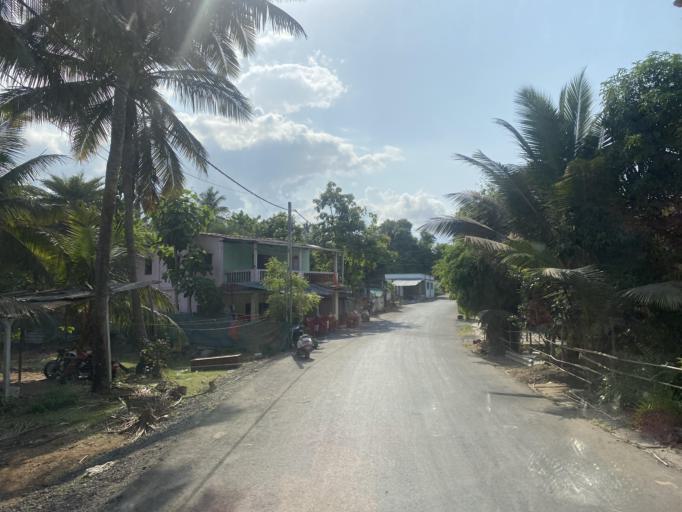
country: IN
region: Daman and Diu
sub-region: Daman District
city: Daman
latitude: 20.3774
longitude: 72.8291
